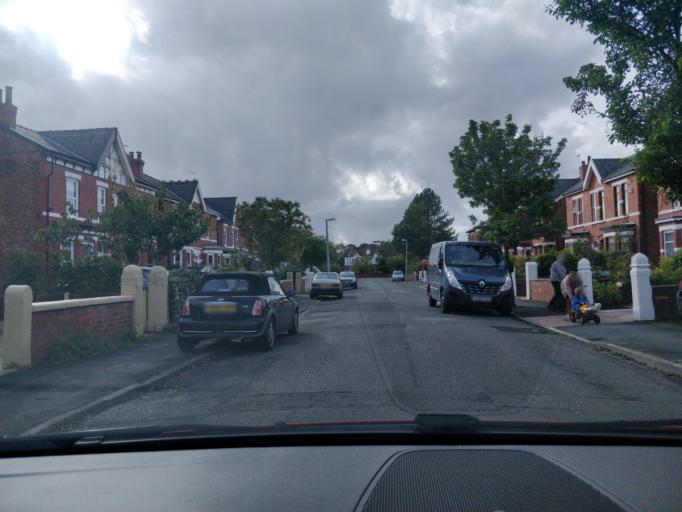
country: GB
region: England
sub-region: Sefton
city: Southport
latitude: 53.6242
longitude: -3.0148
